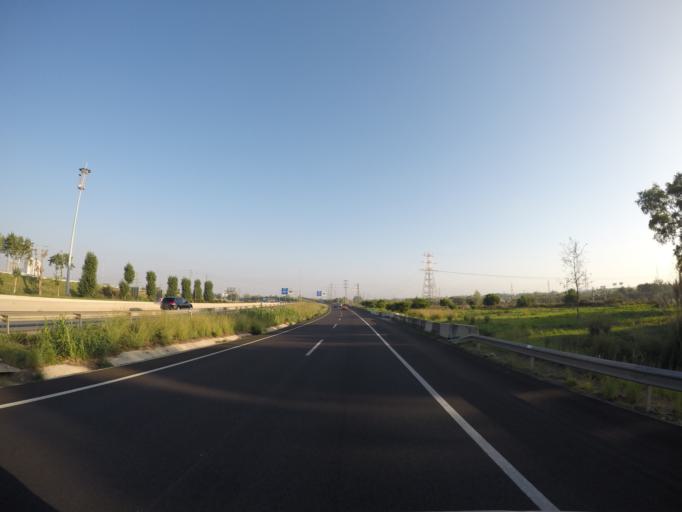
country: ES
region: Catalonia
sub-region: Provincia de Barcelona
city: Cornella de Llobregat
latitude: 41.3425
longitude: 2.0938
